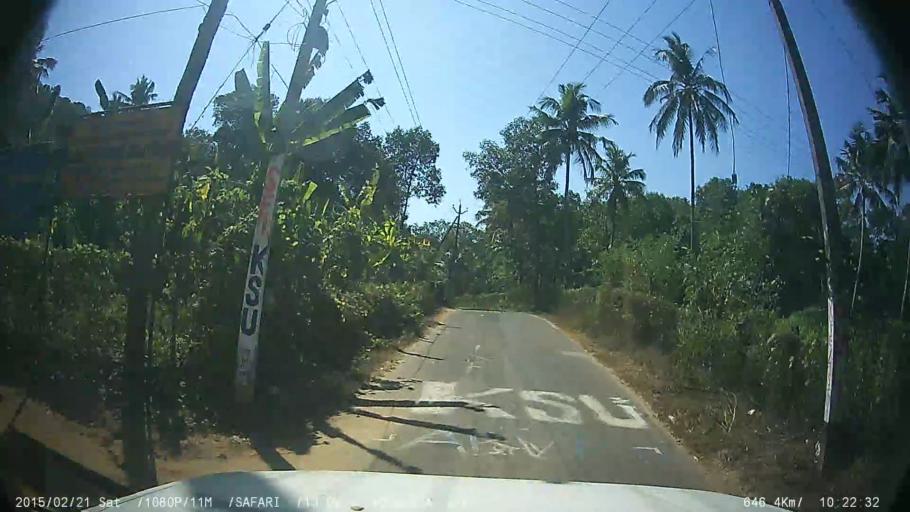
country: IN
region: Kerala
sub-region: Kottayam
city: Palackattumala
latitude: 9.8642
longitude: 76.6713
